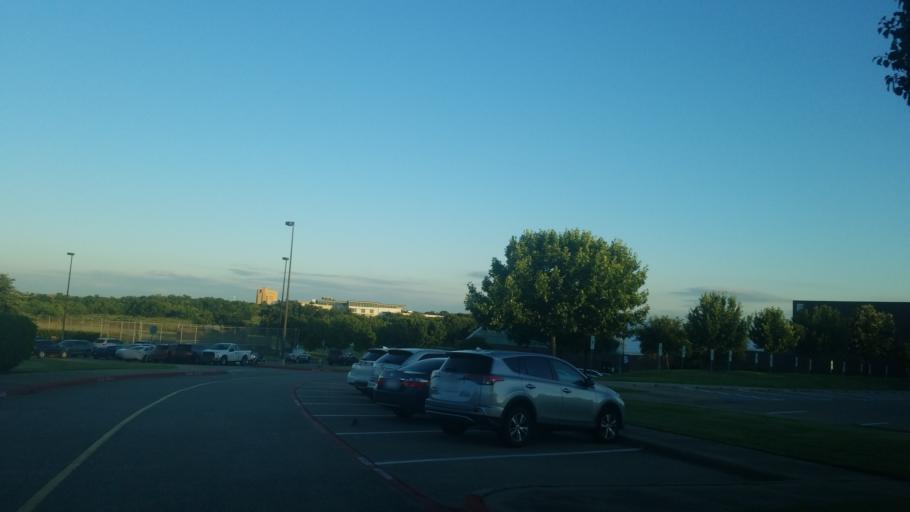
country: US
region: Texas
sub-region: Dallas County
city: Irving
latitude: 32.8735
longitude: -96.9656
